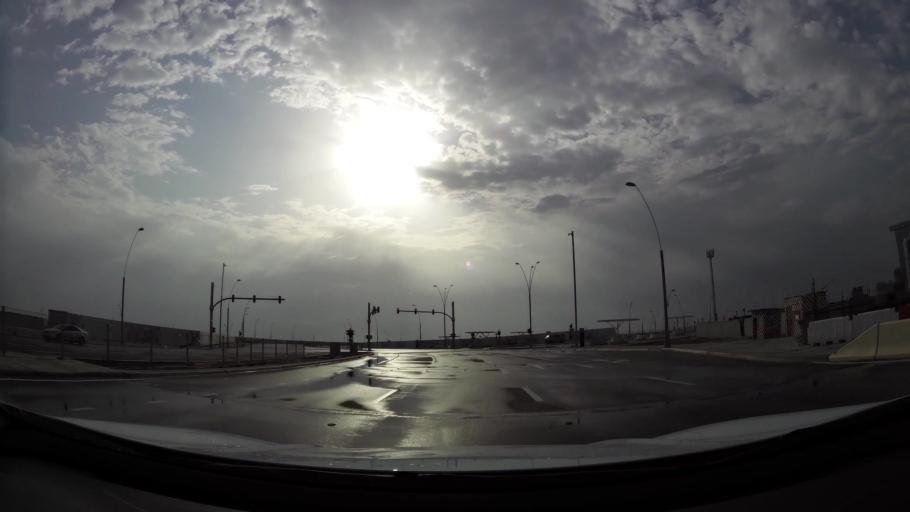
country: AE
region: Abu Dhabi
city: Abu Dhabi
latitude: 24.5077
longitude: 54.4108
